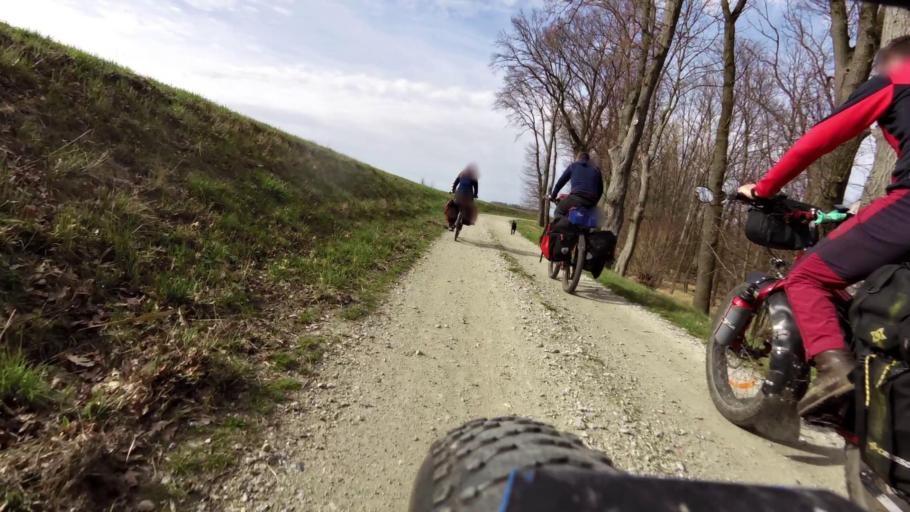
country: DE
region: Brandenburg
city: Reitwein
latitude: 52.5097
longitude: 14.6170
